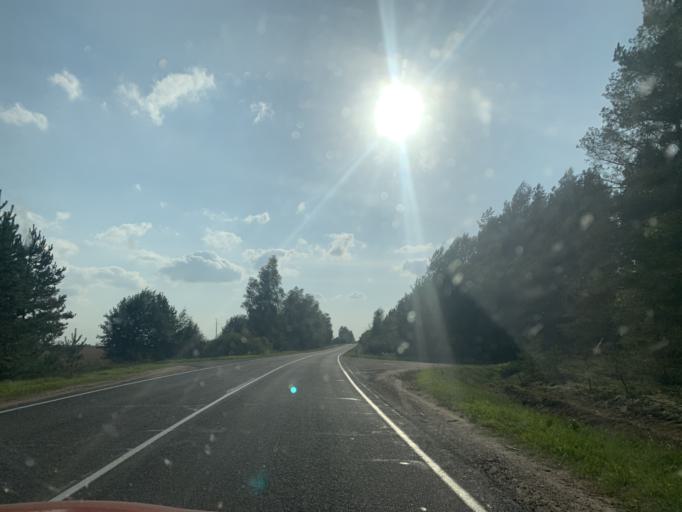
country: BY
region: Minsk
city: Ivyanyets
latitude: 53.8691
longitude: 26.7324
